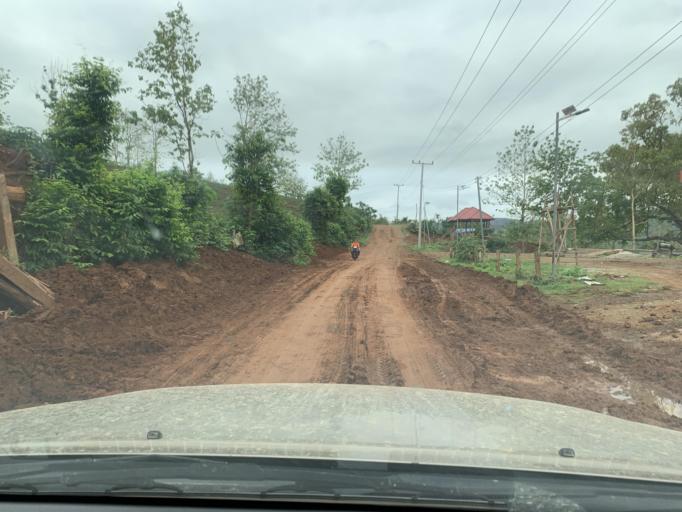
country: TH
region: Nan
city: Mae Charim
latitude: 18.4170
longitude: 101.4458
